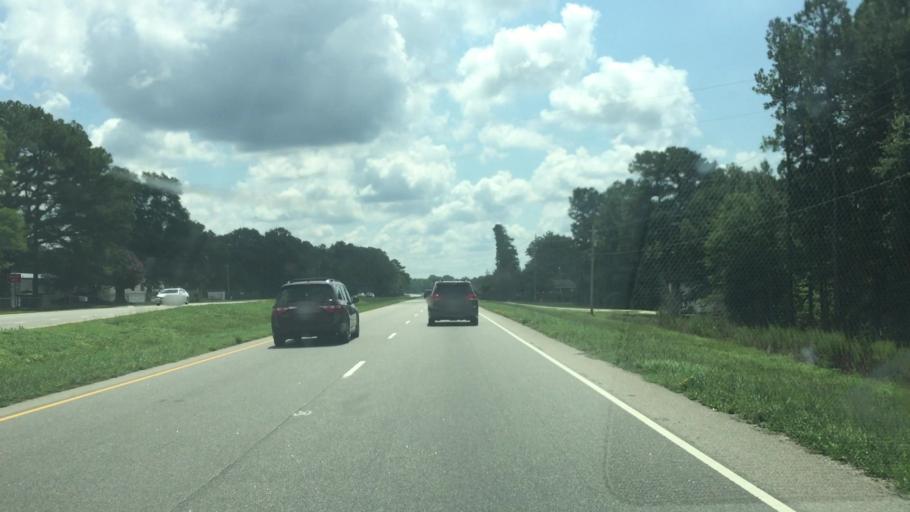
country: US
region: North Carolina
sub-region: Scotland County
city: Laurel Hill
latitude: 34.8219
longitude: -79.5820
